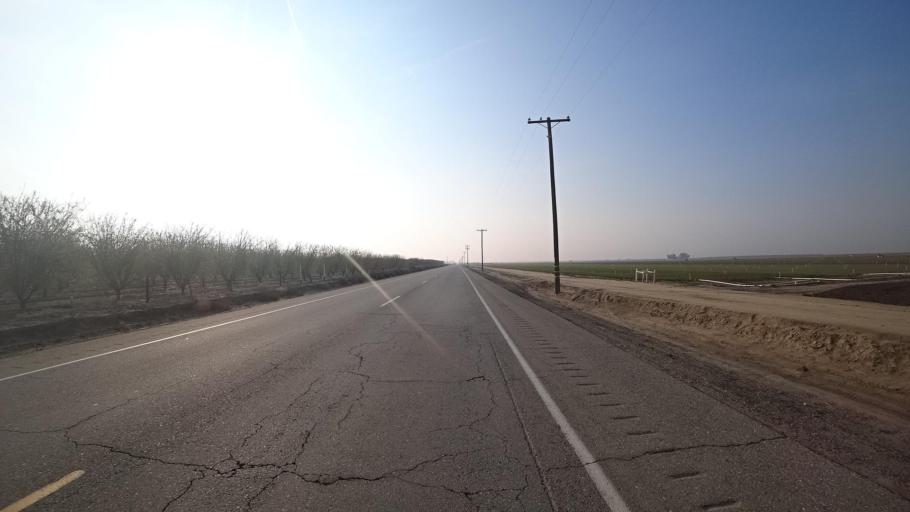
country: US
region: California
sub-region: Kern County
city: Weedpatch
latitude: 35.1622
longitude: -118.9146
